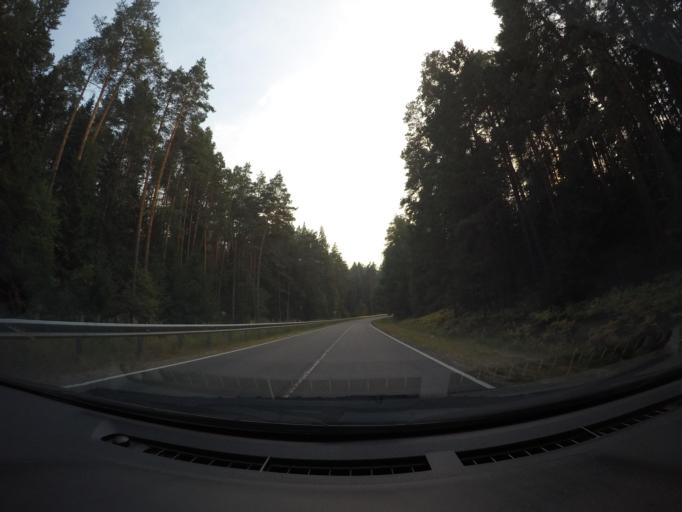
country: RU
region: Moskovskaya
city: Imeni Tsyurupy
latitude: 55.5044
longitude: 38.7142
